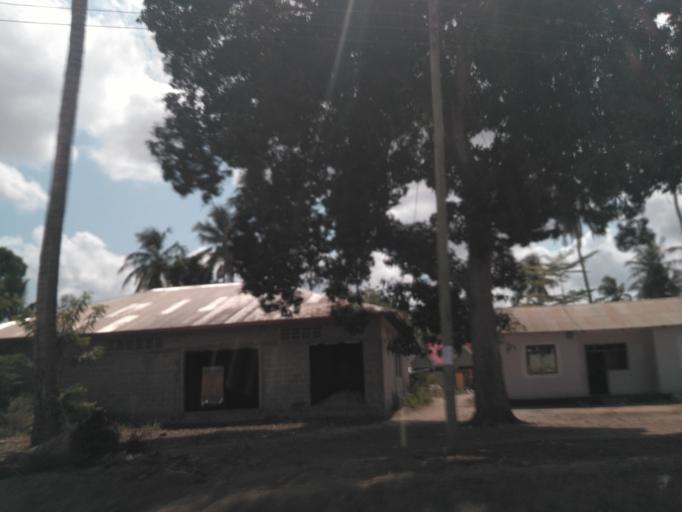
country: TZ
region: Dar es Salaam
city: Dar es Salaam
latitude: -6.8849
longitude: 39.3377
